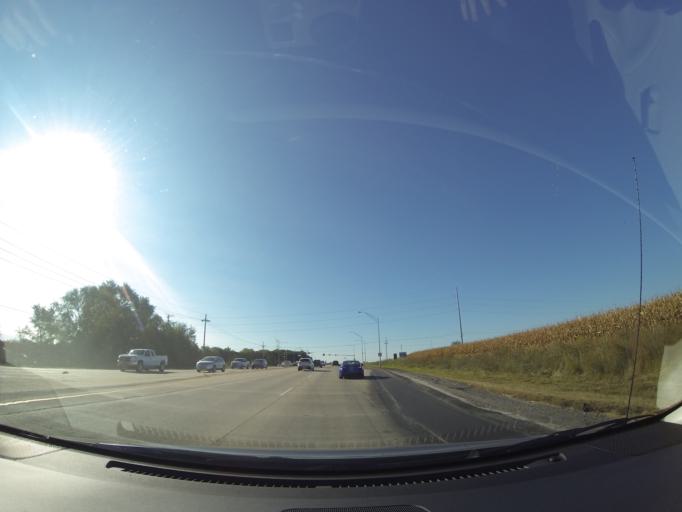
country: US
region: Nebraska
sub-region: Sarpy County
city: Gretna
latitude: 41.2065
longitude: -96.2345
